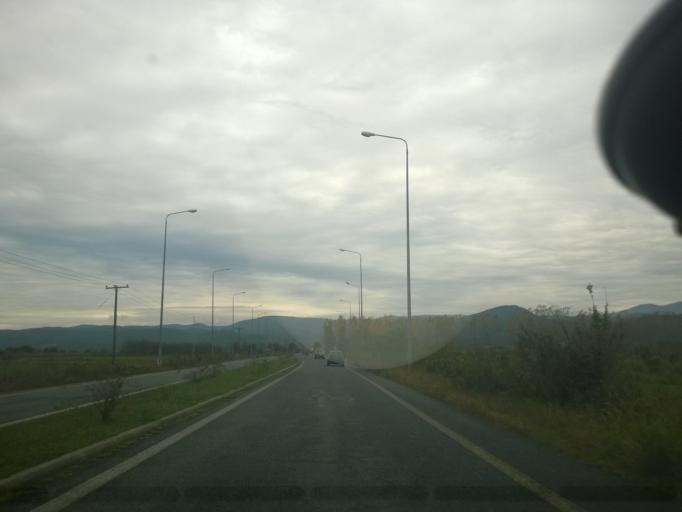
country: GR
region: Central Macedonia
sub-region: Nomos Pellis
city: Apsalos
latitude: 40.9165
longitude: 22.0760
